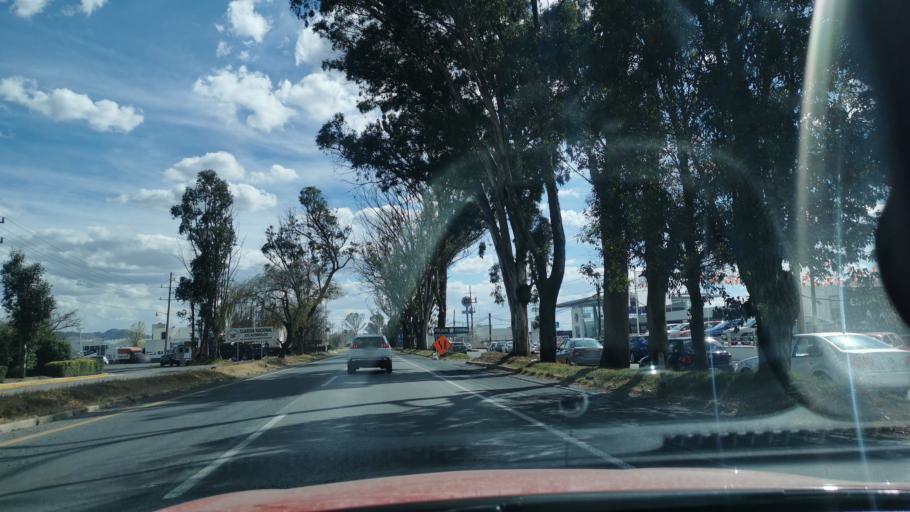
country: MX
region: Mexico
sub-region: Atlacomulco
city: Tecoac (Santa Maria Nativitas)
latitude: 19.7862
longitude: -99.8666
